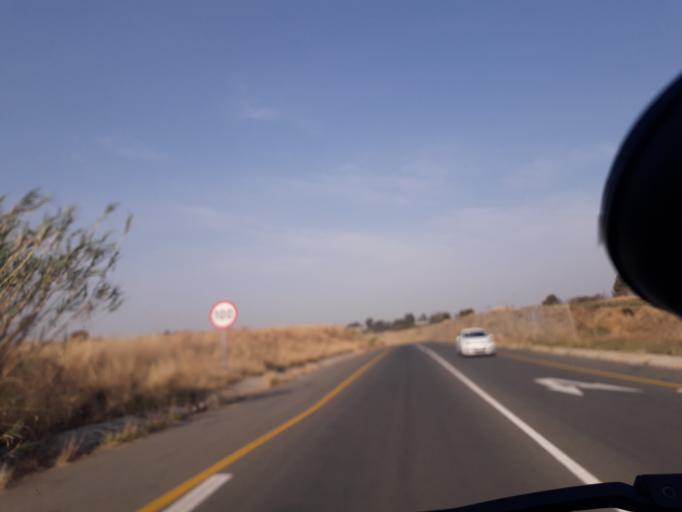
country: ZA
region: Gauteng
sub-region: West Rand District Municipality
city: Muldersdriseloop
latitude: -25.9701
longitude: 27.9117
